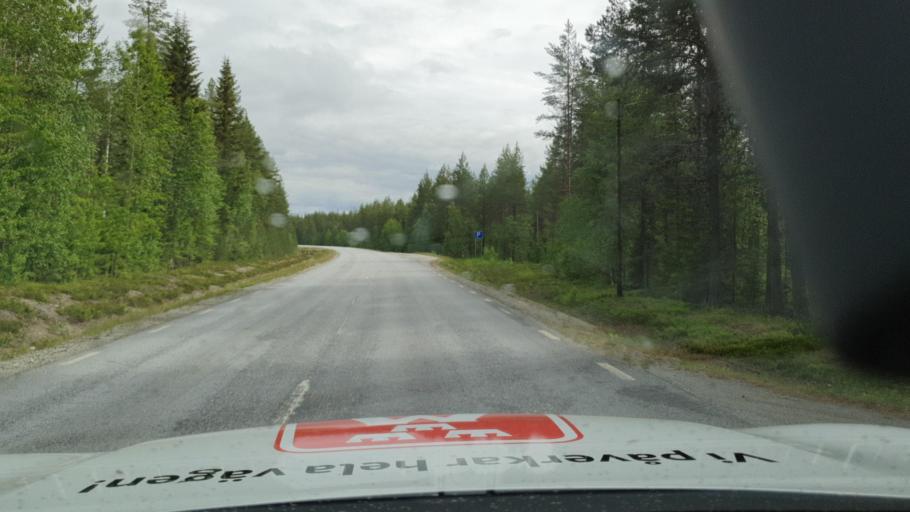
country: SE
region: Vaesterbotten
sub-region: Asele Kommun
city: Asele
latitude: 64.1943
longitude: 17.0804
